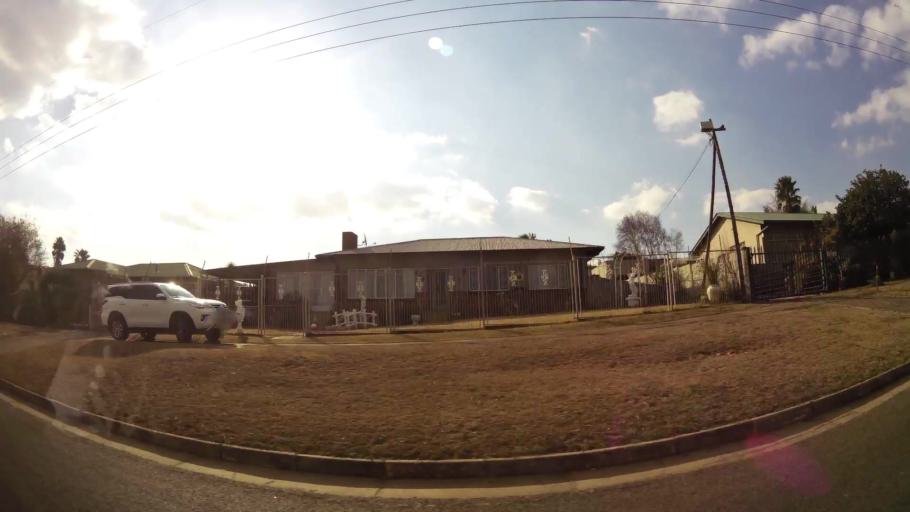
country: ZA
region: Gauteng
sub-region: West Rand District Municipality
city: Krugersdorp
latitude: -26.0855
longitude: 27.7635
